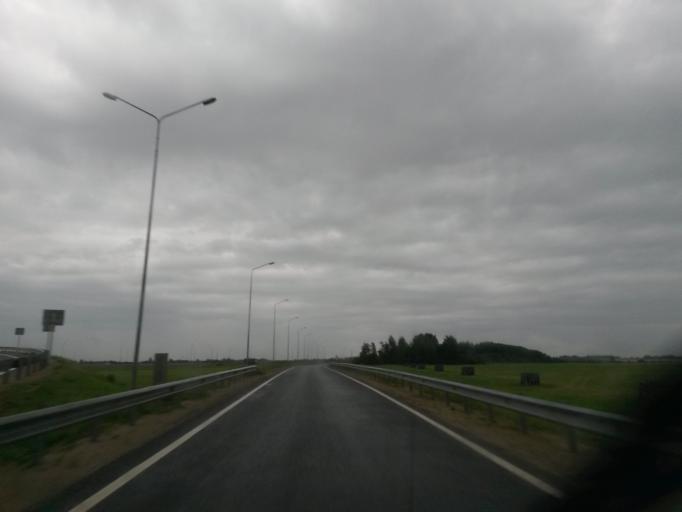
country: RU
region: Jaroslavl
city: Yaroslavl
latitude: 57.7395
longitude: 39.8922
